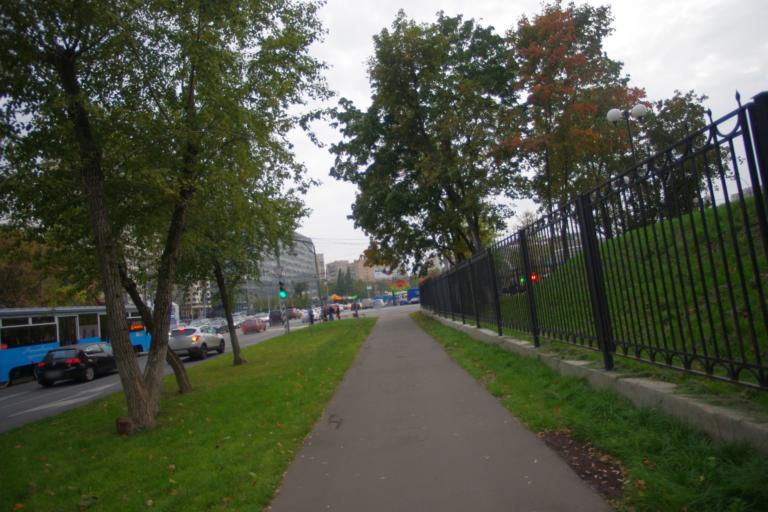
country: RU
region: Moskovskaya
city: Semenovskoye
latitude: 55.6848
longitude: 37.5529
